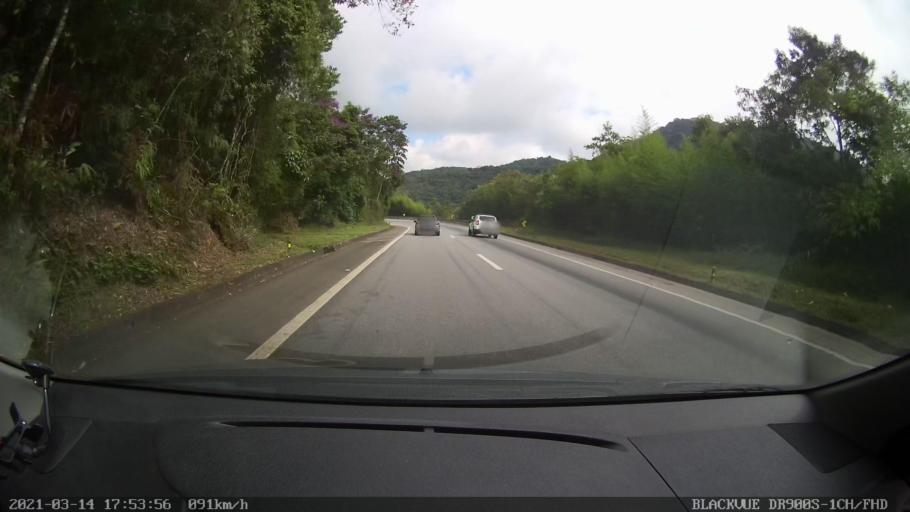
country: BR
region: Rio de Janeiro
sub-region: Petropolis
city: Petropolis
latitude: -22.4840
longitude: -43.2309
